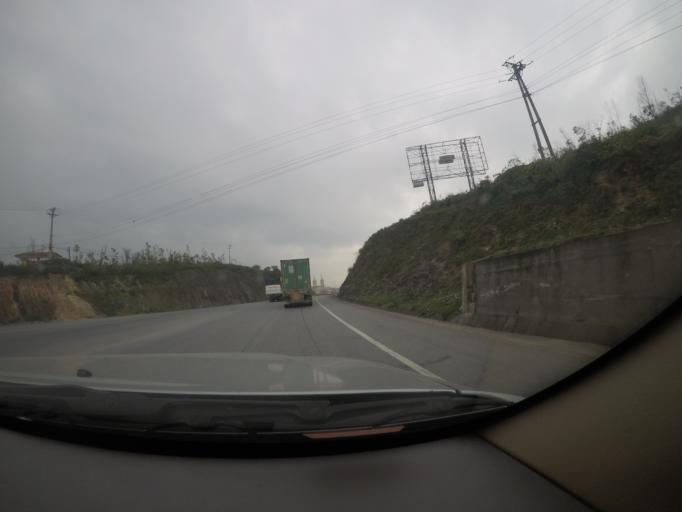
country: VN
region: Ha Tinh
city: Ky Anh
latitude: 17.9950
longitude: 106.4660
